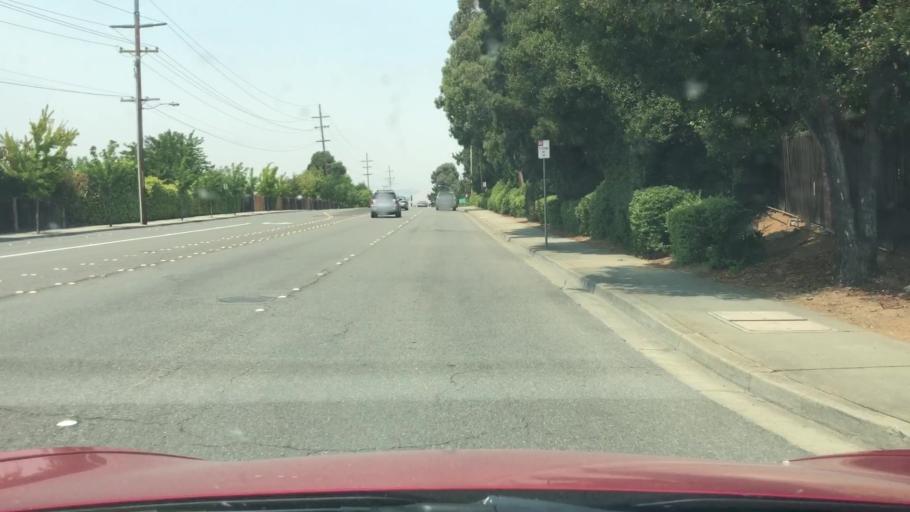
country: US
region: California
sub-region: Alameda County
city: Livermore
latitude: 37.6640
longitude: -121.7802
